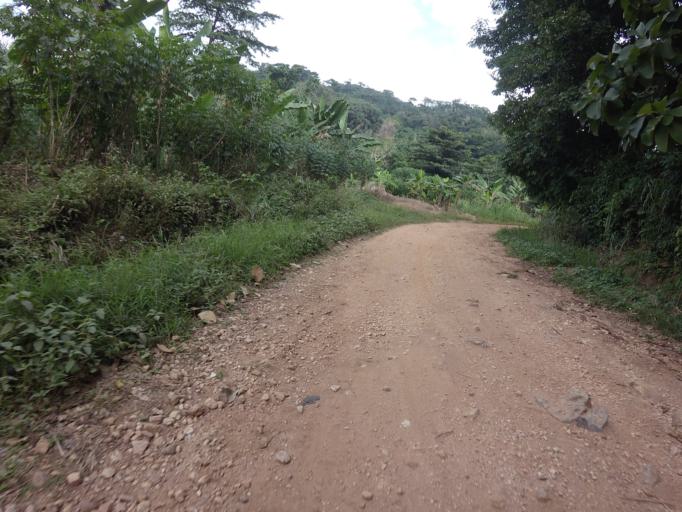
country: GH
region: Volta
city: Kpandu
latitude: 6.8887
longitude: 0.4381
